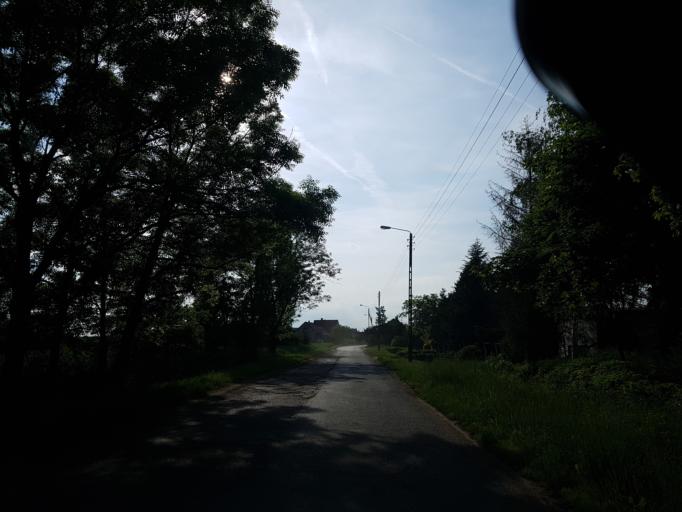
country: PL
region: Lower Silesian Voivodeship
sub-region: Powiat strzelinski
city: Wiazow
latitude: 50.8404
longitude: 17.2208
